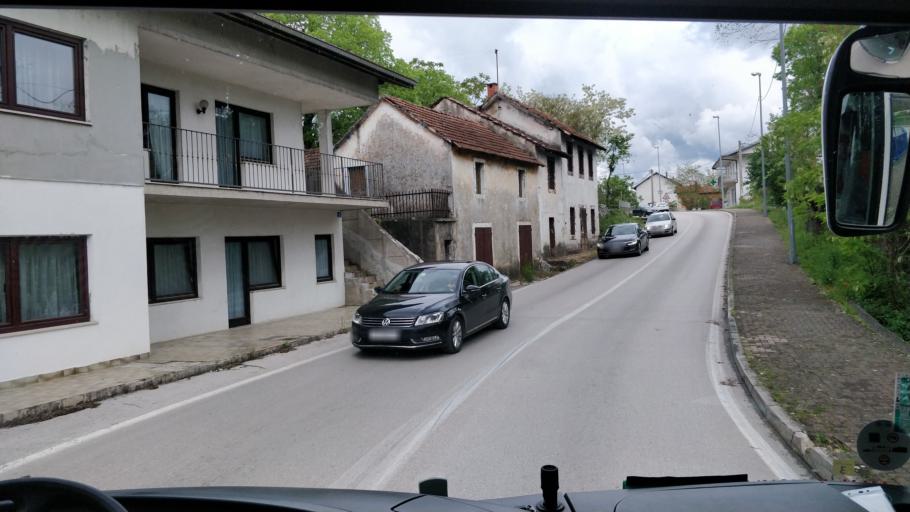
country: BA
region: Federation of Bosnia and Herzegovina
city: Ljubuski
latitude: 43.1838
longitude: 17.5232
